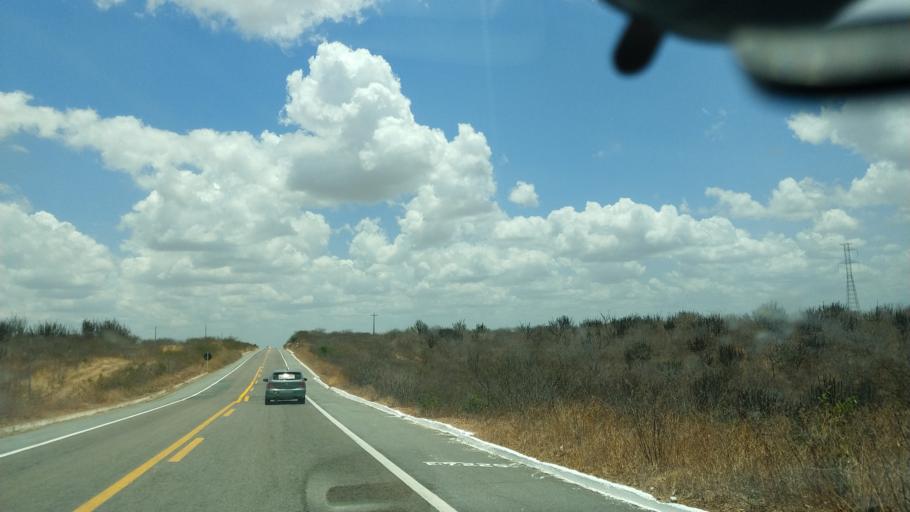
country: BR
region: Rio Grande do Norte
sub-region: Cerro Cora
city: Cerro Cora
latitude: -6.1952
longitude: -36.2636
